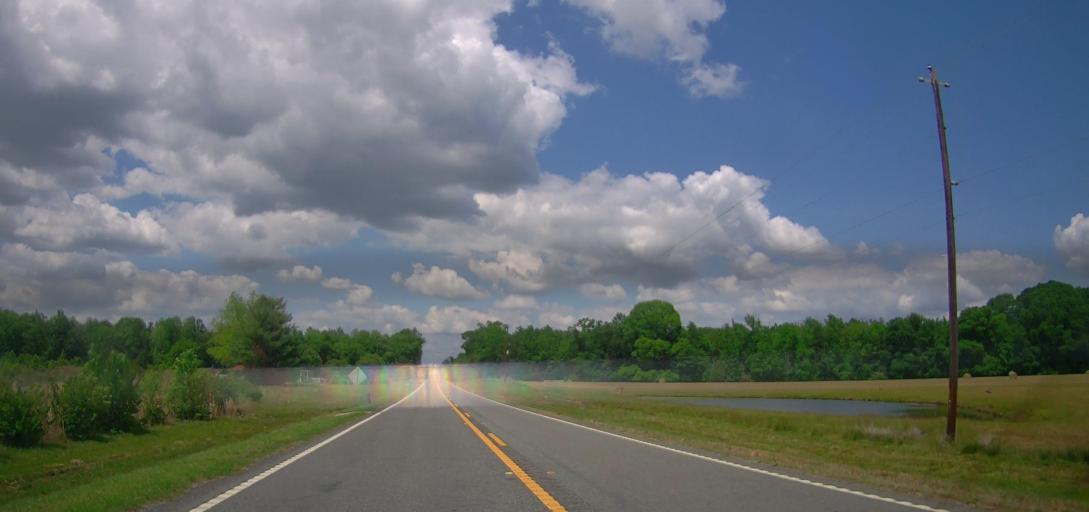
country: US
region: Georgia
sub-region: Treutlen County
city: Soperton
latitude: 32.4045
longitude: -82.6059
